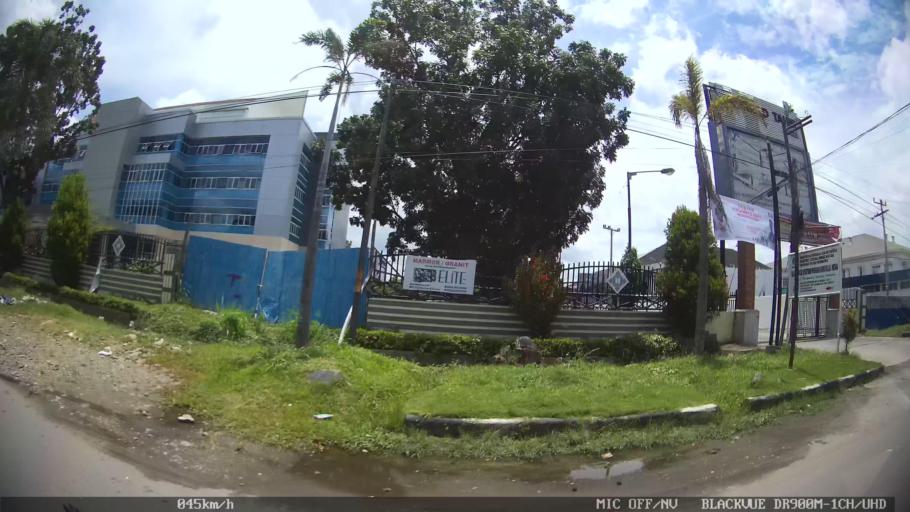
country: ID
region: North Sumatra
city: Medan
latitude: 3.6139
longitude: 98.7169
